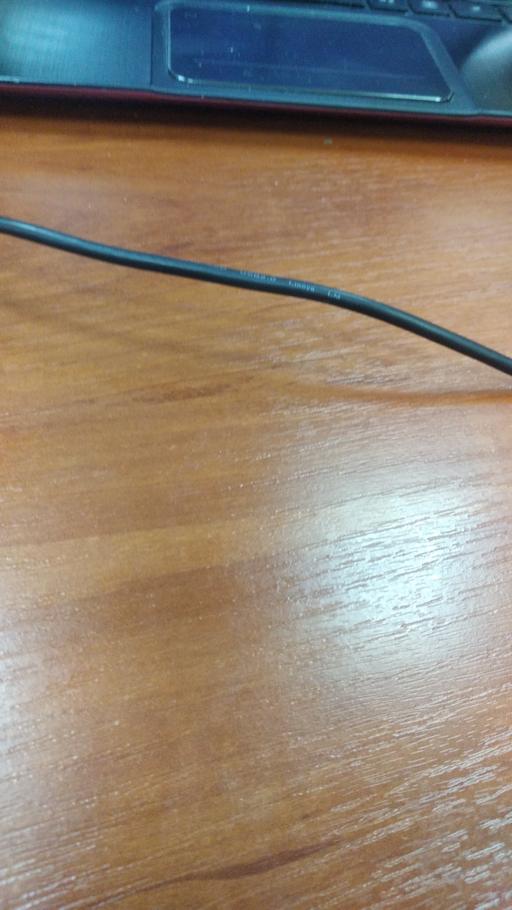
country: RU
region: Moscow
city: Vagonoremont
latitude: 55.9056
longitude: 37.5583
